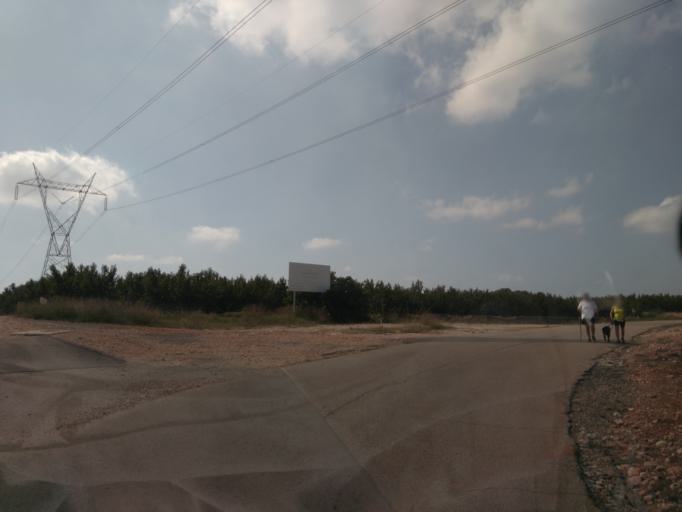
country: ES
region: Valencia
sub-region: Provincia de Valencia
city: Masalaves
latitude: 39.1715
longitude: -0.5535
